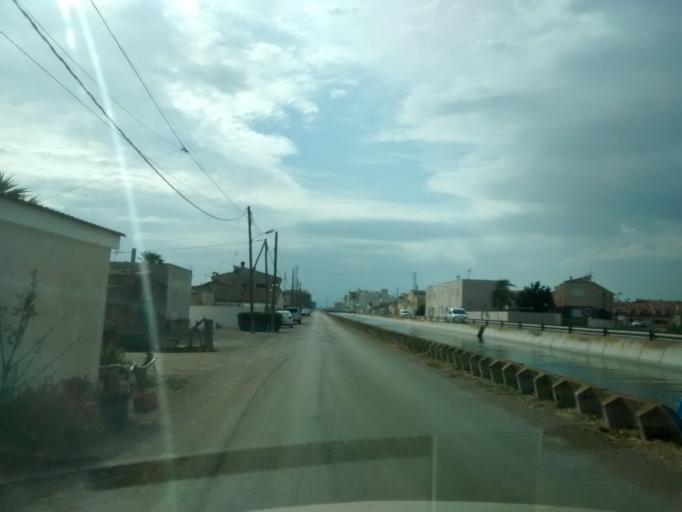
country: ES
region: Catalonia
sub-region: Provincia de Tarragona
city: Deltebre
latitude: 40.7029
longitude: 0.7229
